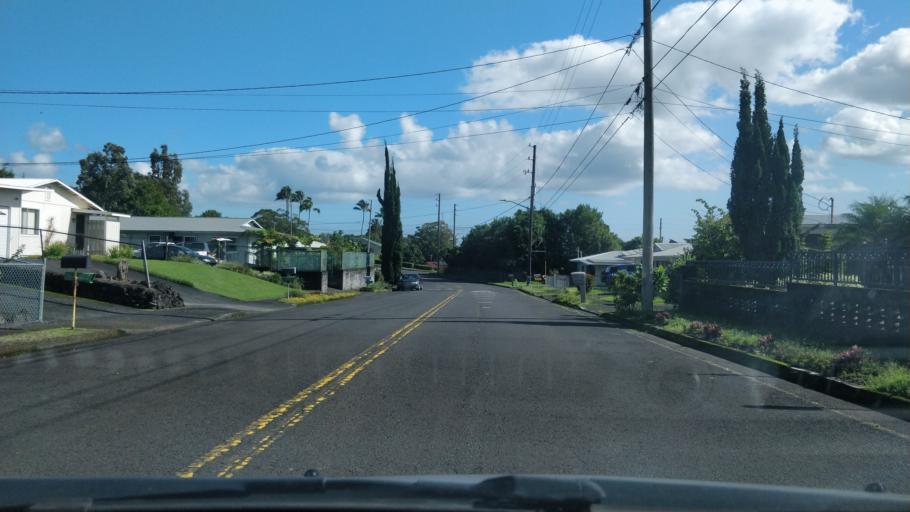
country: US
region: Hawaii
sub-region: Hawaii County
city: Hilo
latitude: 19.6791
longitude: -155.0878
